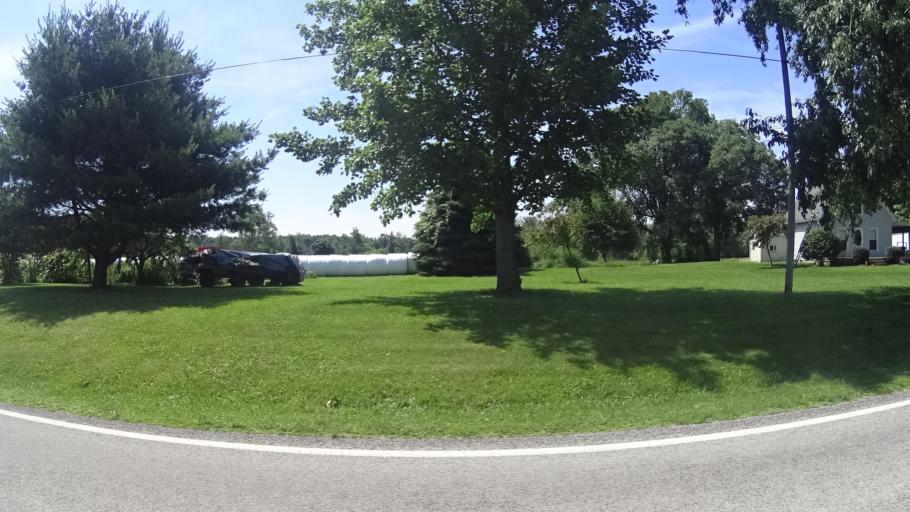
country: US
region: Ohio
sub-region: Huron County
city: Wakeman
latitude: 41.3451
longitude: -82.4521
